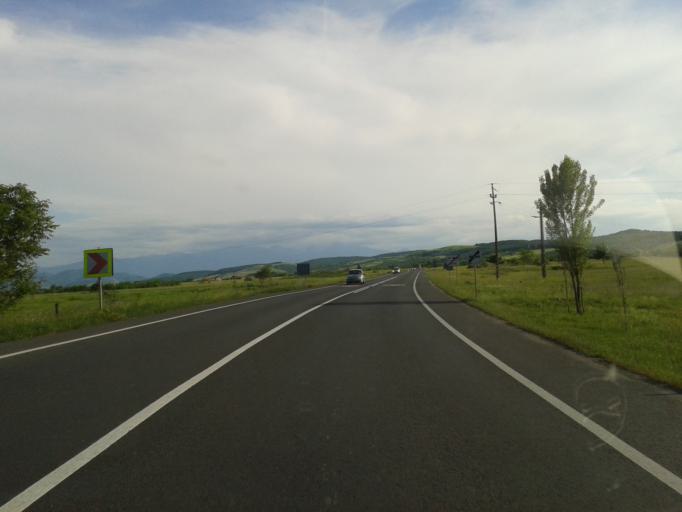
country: RO
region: Hunedoara
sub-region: Comuna Calan
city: Calan
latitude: 45.7127
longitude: 22.9929
